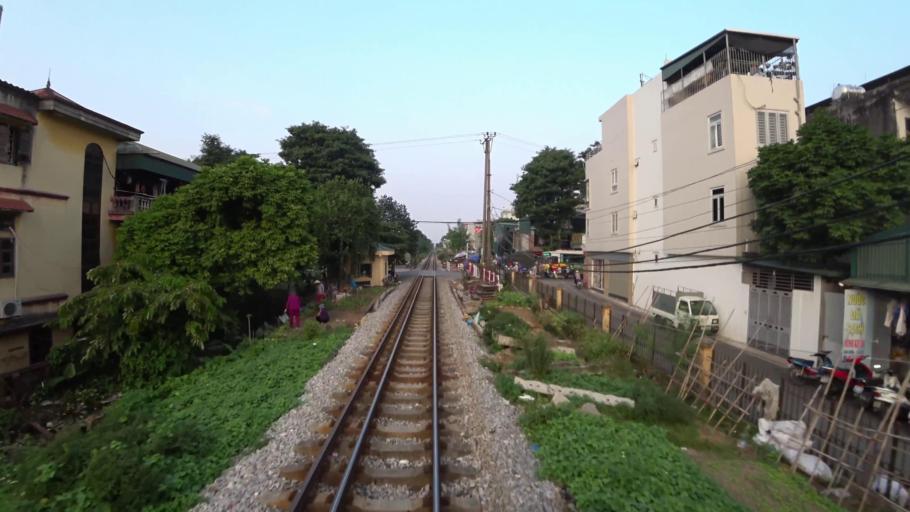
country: VN
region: Ha Noi
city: Trau Quy
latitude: 21.0809
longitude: 105.9117
